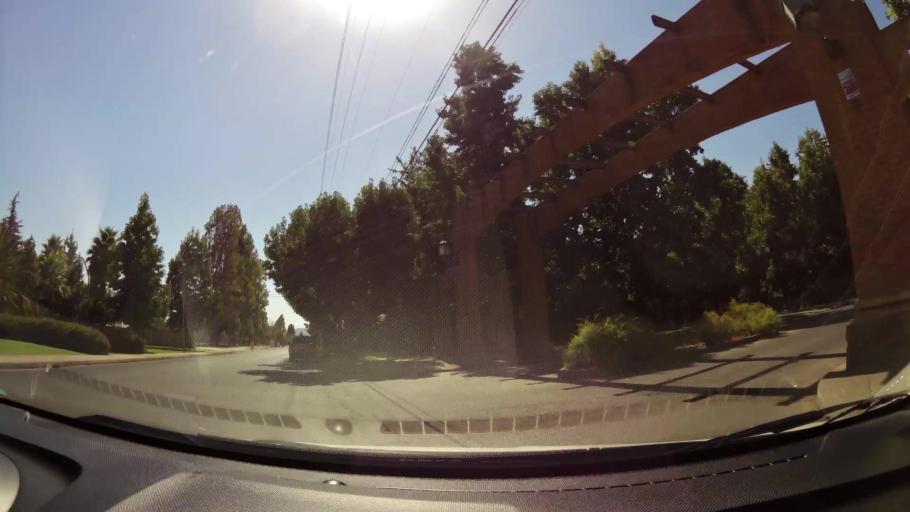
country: CL
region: Maule
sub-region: Provincia de Talca
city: Talca
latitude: -35.4349
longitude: -71.6159
